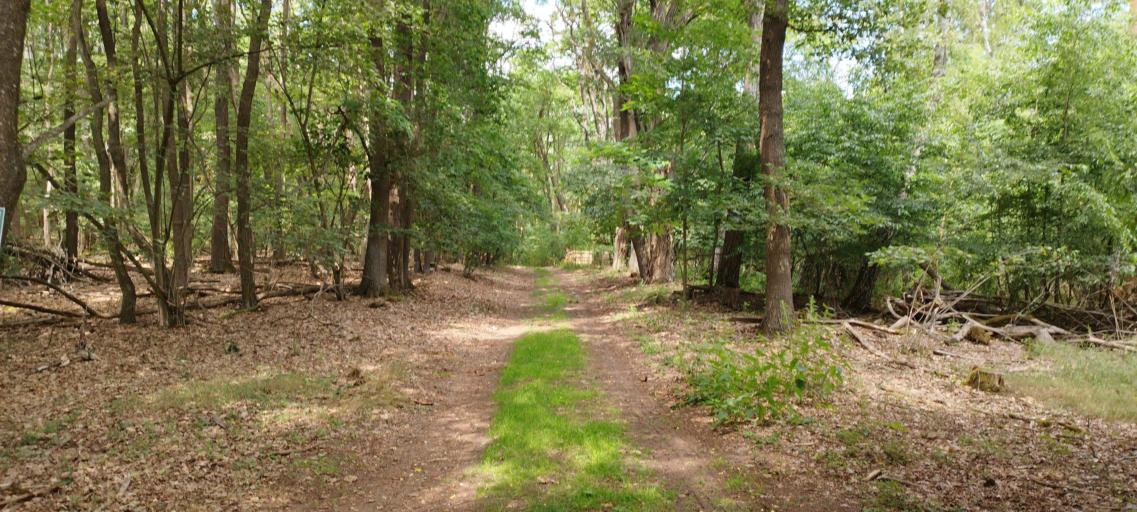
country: DE
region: Brandenburg
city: Bad Saarow
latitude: 52.2960
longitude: 14.0329
